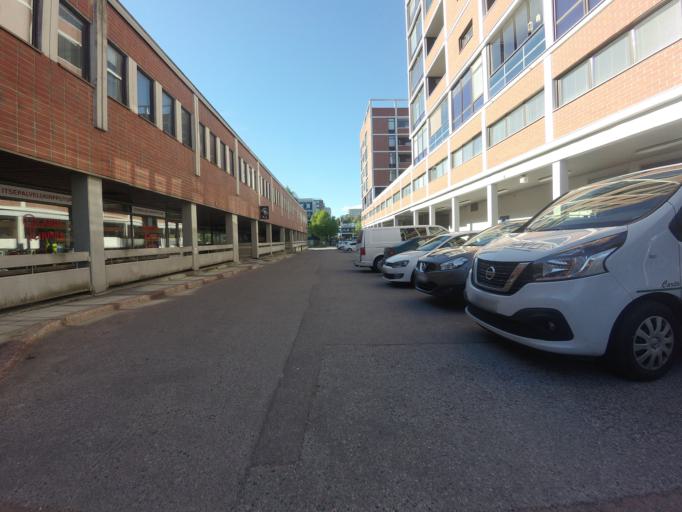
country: FI
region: Uusimaa
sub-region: Helsinki
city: Kauniainen
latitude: 60.1718
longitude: 24.7256
